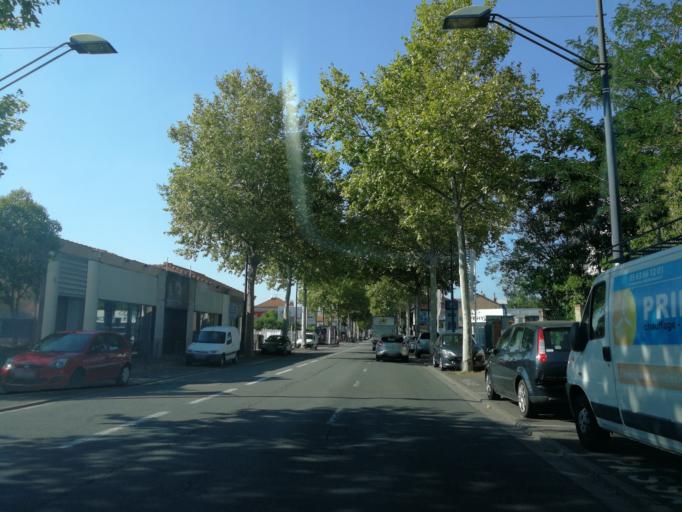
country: FR
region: Midi-Pyrenees
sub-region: Departement de la Haute-Garonne
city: Toulouse
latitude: 43.6340
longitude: 1.4312
